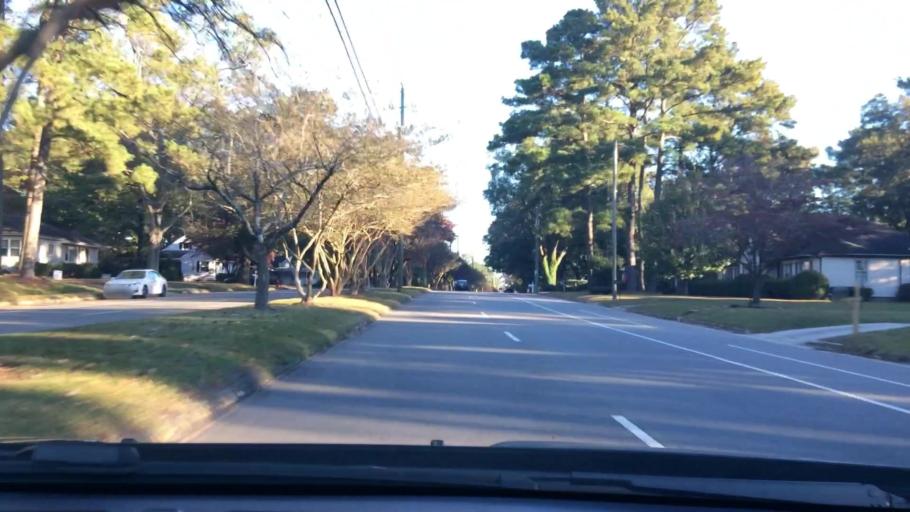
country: US
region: North Carolina
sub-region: Pitt County
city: Greenville
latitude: 35.5938
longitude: -77.3607
